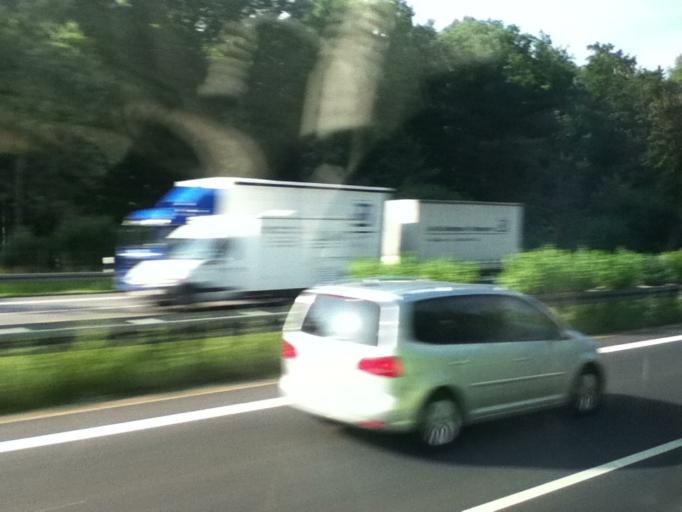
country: DE
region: Saxony
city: Nossen
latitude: 51.0249
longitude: 13.2631
